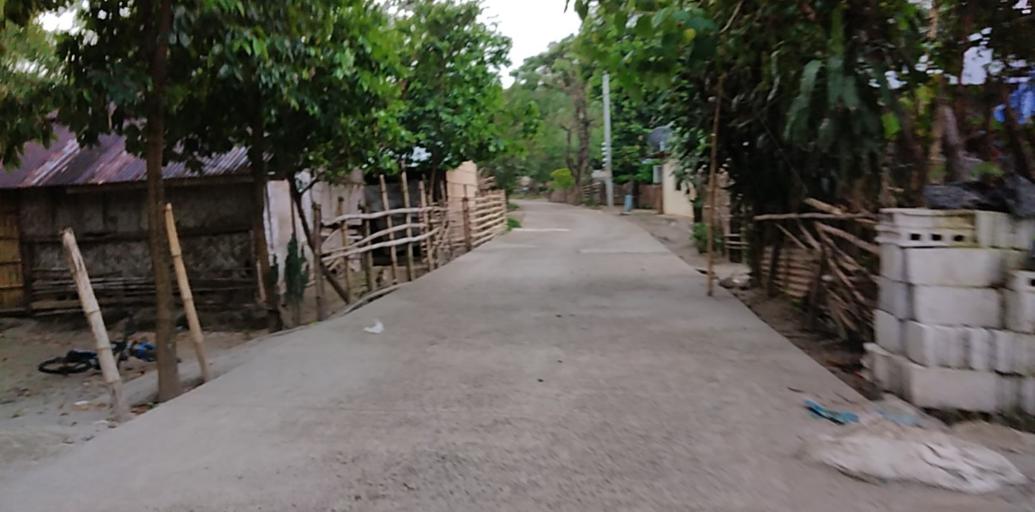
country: PH
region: Central Luzon
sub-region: Province of Pampanga
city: Babo-Pangulo
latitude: 15.1093
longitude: 120.4917
